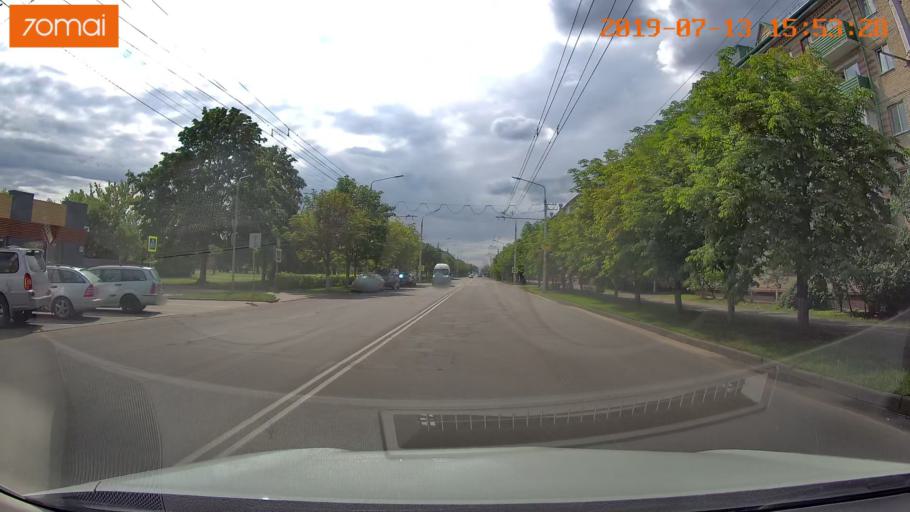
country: BY
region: Mogilev
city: Babruysk
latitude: 53.1388
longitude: 29.2078
